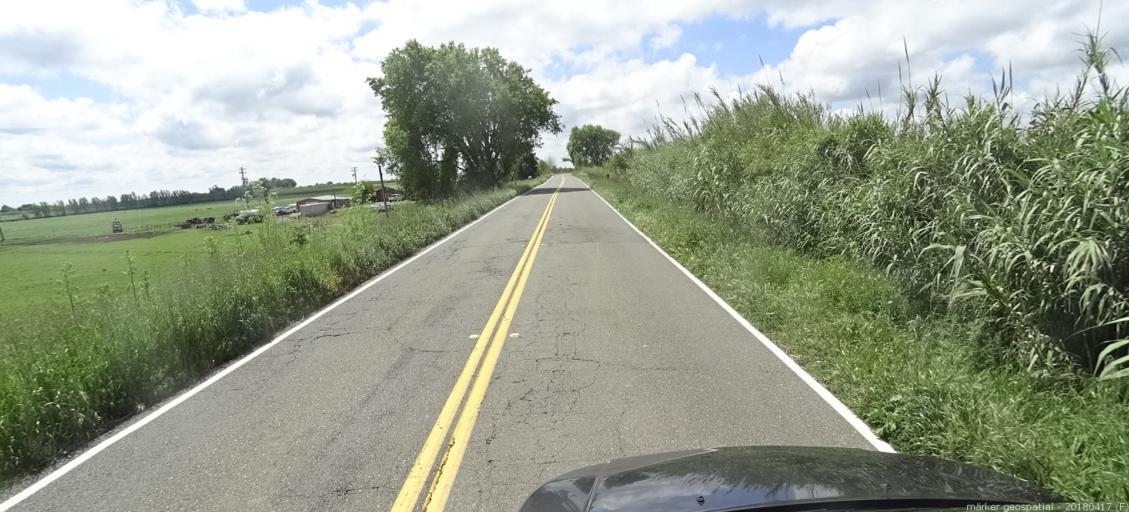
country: US
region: California
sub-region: Sacramento County
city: Walnut Grove
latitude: 38.2029
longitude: -121.5569
